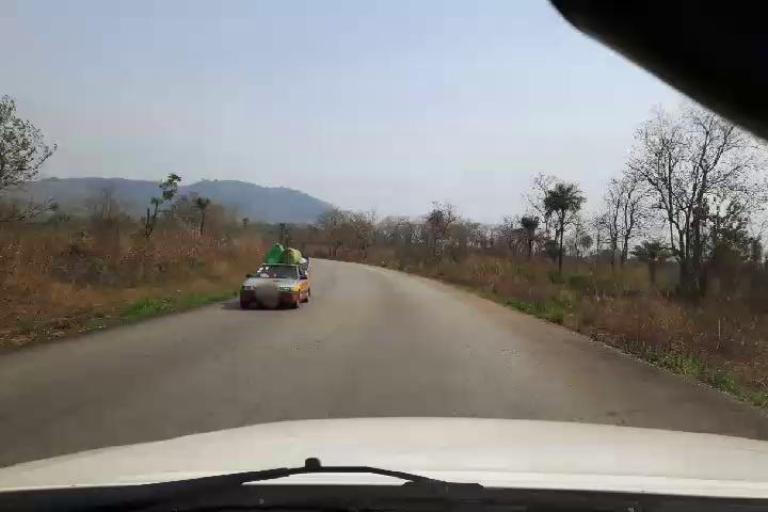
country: SL
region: Northern Province
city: Yonibana
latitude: 8.3942
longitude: -12.1935
